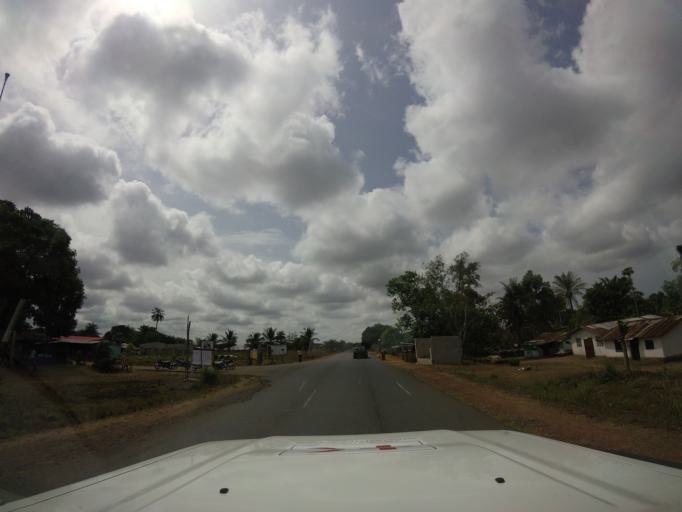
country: LR
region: Montserrado
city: Monrovia
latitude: 6.4711
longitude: -10.8095
